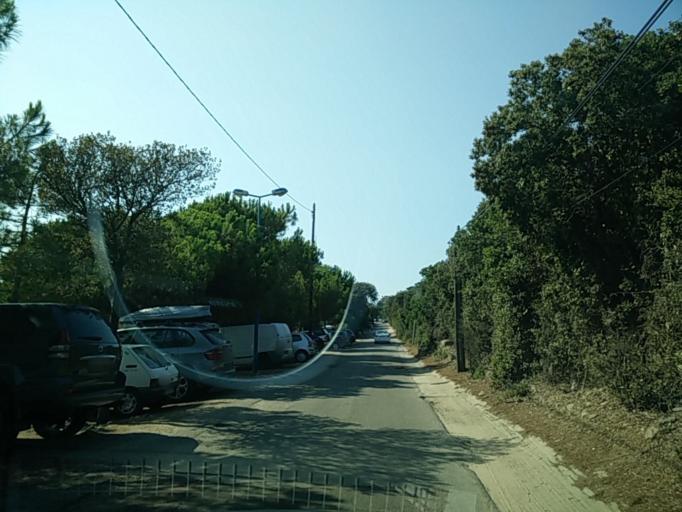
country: FR
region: Corsica
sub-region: Departement de la Corse-du-Sud
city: Pietrosella
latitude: 41.8435
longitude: 8.7666
